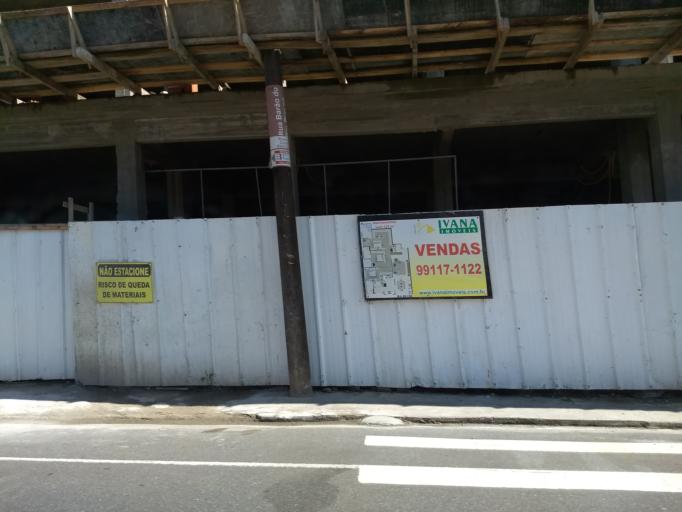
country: BR
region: Santa Catarina
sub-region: Jaragua Do Sul
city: Jaragua do Sul
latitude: -26.4916
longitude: -49.0773
